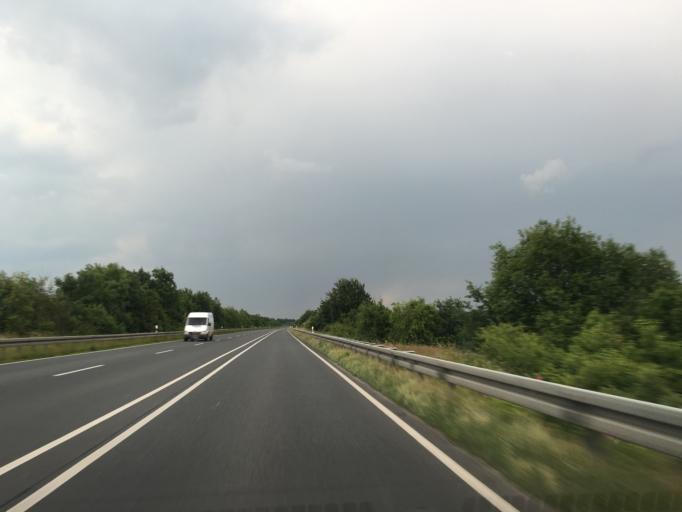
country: DE
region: North Rhine-Westphalia
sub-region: Regierungsbezirk Munster
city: Ochtrup
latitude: 52.1918
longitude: 7.2096
